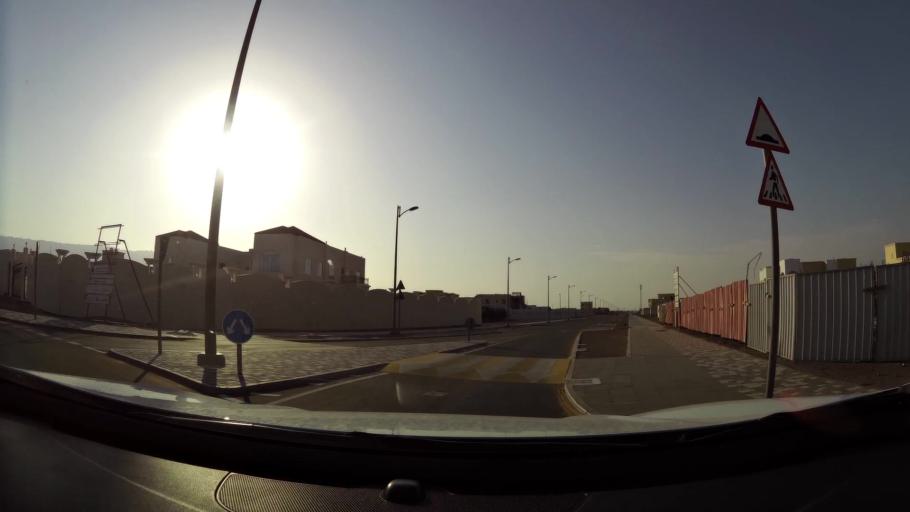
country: AE
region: Abu Dhabi
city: Al Ain
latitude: 24.0954
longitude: 55.8531
